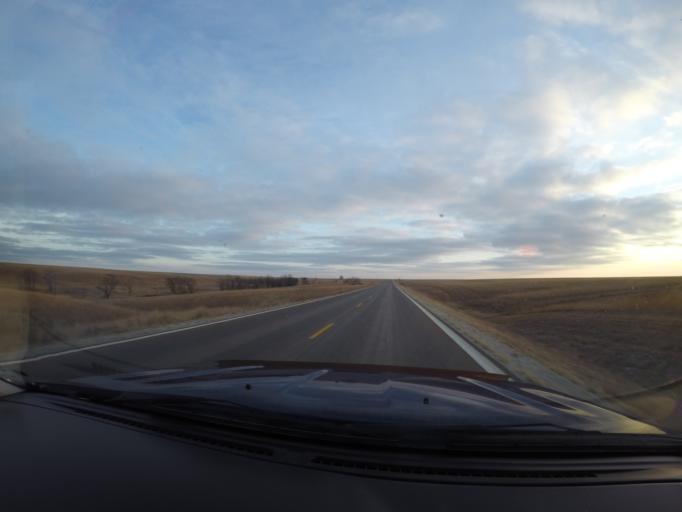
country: US
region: Kansas
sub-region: Morris County
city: Council Grove
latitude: 38.5584
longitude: -96.5219
